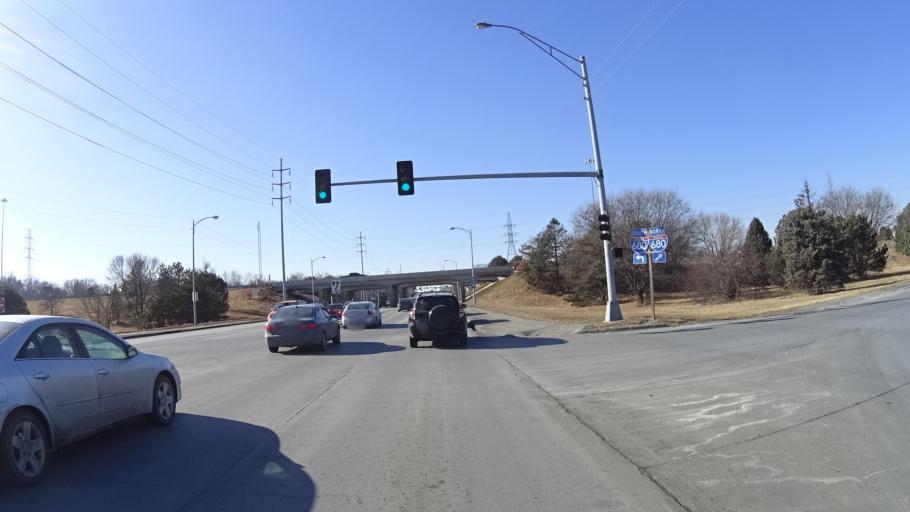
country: US
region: Nebraska
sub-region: Douglas County
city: Ralston
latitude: 41.3068
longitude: -96.0692
